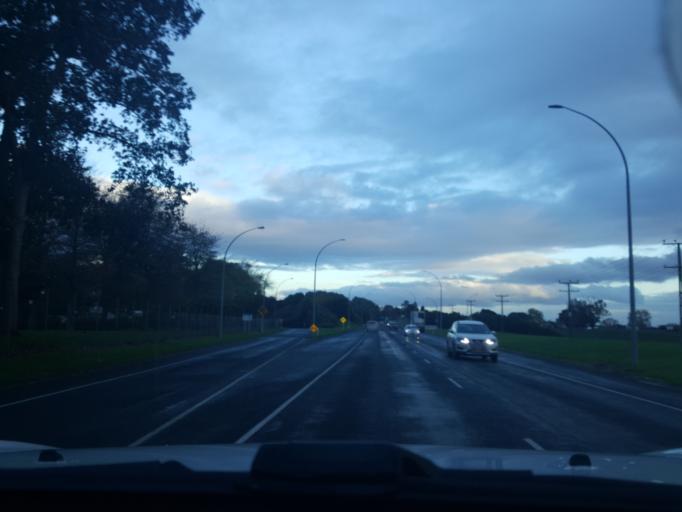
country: NZ
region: Waikato
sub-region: Waikato District
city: Ngaruawahia
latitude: -37.7180
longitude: 175.2135
